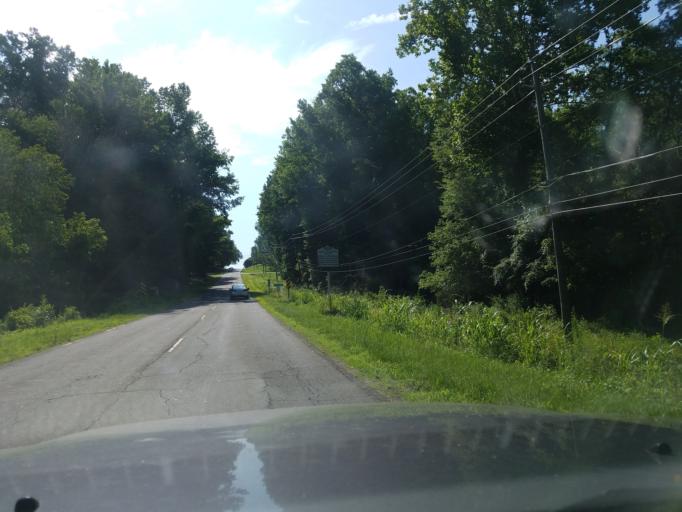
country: US
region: North Carolina
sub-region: Granville County
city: Oxford
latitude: 36.3143
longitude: -78.5639
